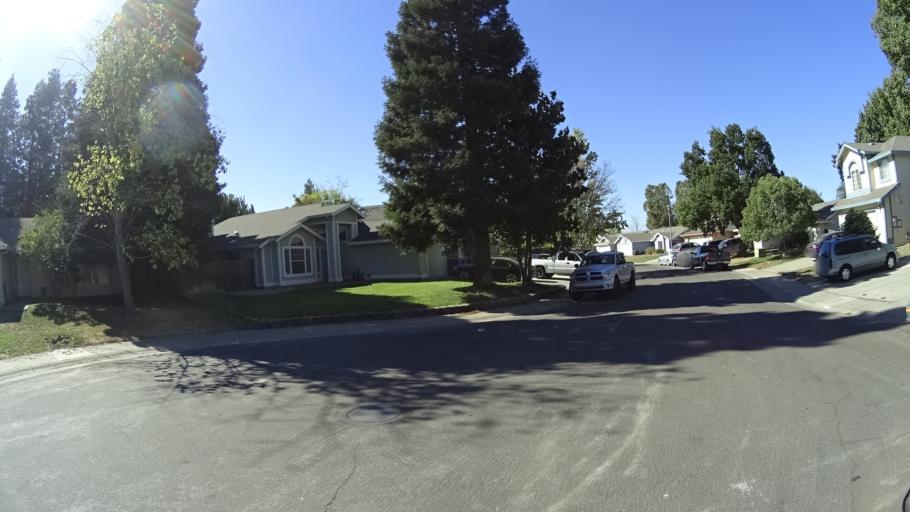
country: US
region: California
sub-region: Sacramento County
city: Parkway
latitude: 38.4660
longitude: -121.4489
